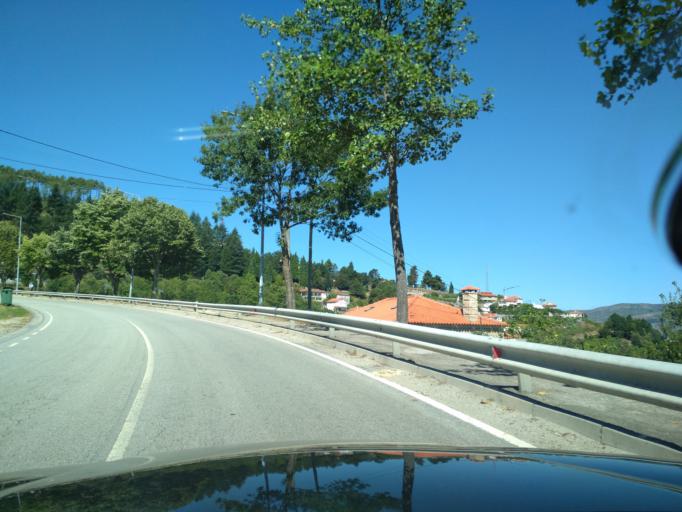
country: PT
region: Vila Real
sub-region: Ribeira de Pena
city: Ribeira de Pena
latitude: 41.5189
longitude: -7.8016
